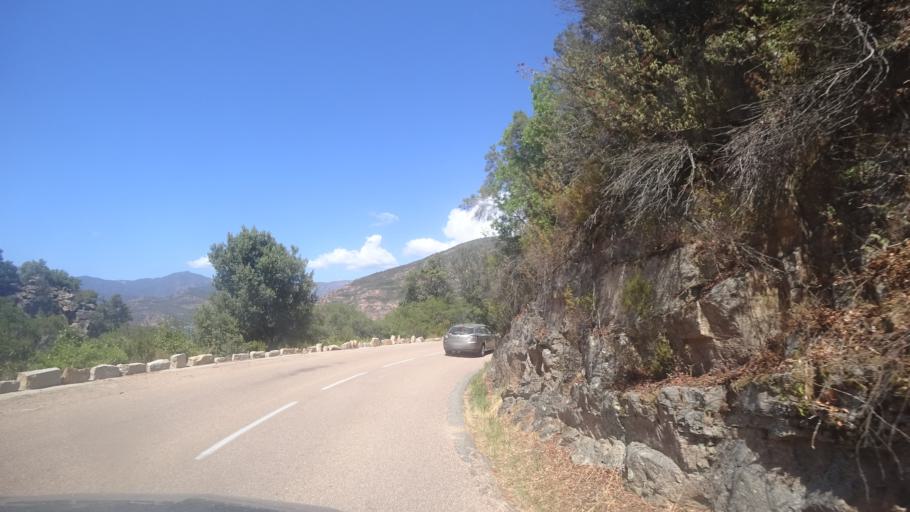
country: FR
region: Corsica
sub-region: Departement de la Corse-du-Sud
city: Cargese
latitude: 42.2603
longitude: 8.6892
